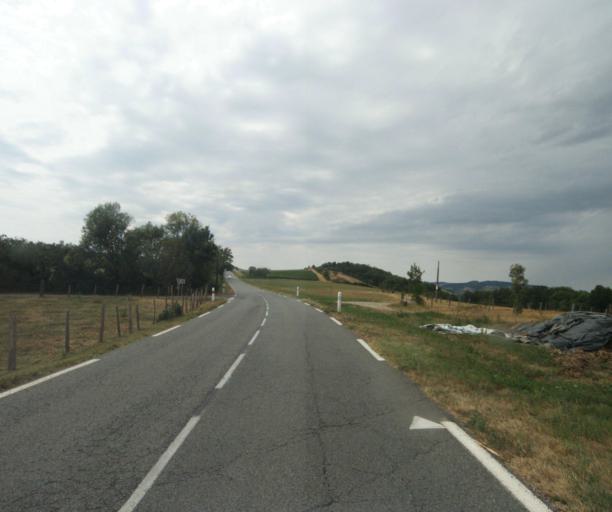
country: FR
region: Rhone-Alpes
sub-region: Departement du Rhone
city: Saint-Verand
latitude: 45.8954
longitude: 4.5513
